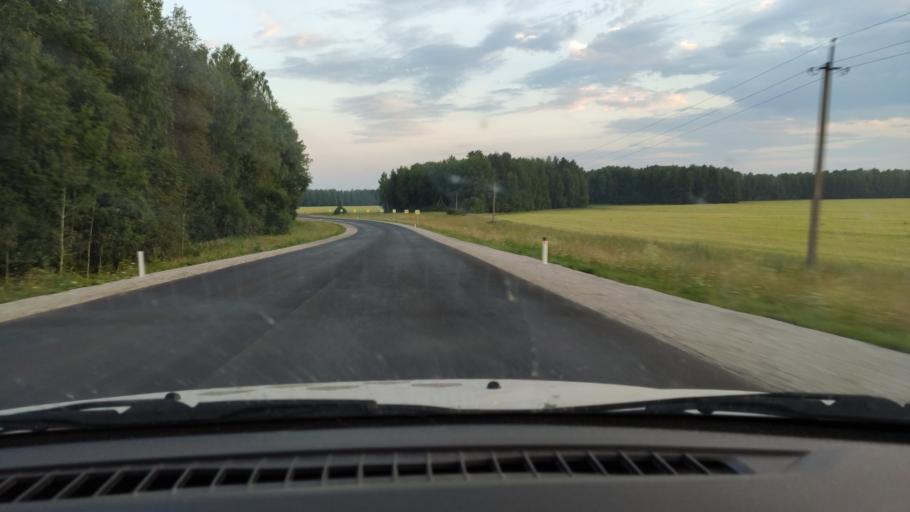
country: RU
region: Perm
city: Zyukayka
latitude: 58.2939
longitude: 54.7997
